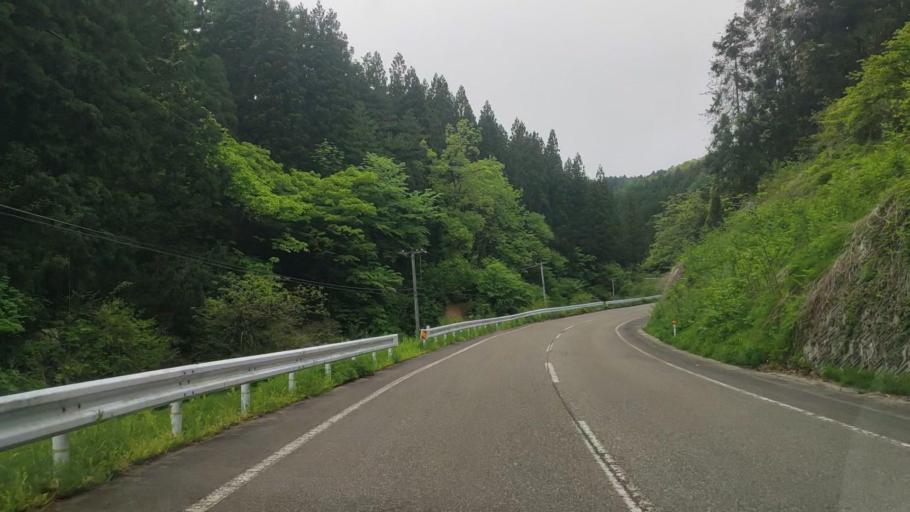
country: JP
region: Niigata
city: Gosen
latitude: 37.7132
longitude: 139.1192
